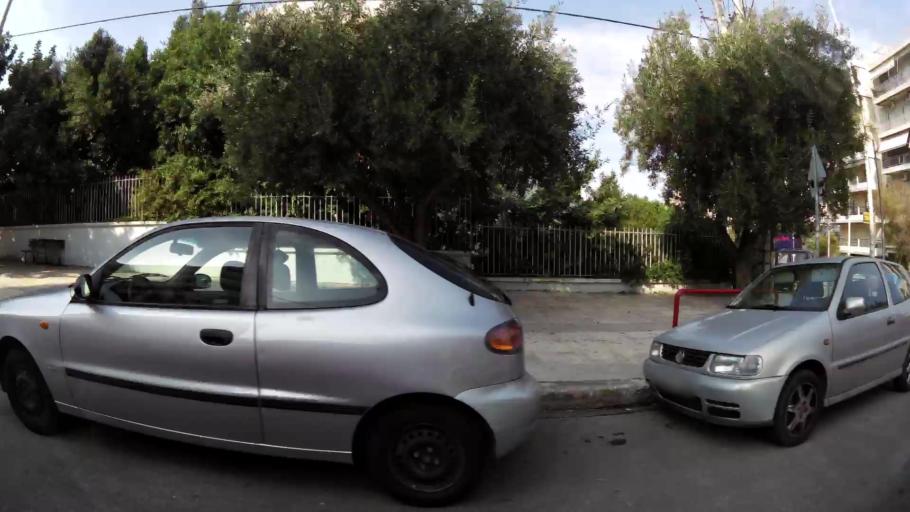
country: GR
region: Attica
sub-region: Nomarchia Athinas
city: Nea Smyrni
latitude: 37.9435
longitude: 23.7068
